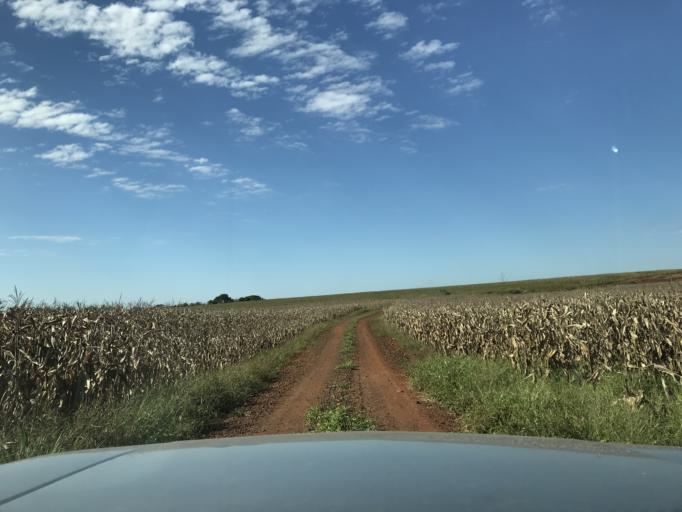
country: BR
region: Parana
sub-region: Ipora
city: Ipora
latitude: -24.1539
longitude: -53.7439
